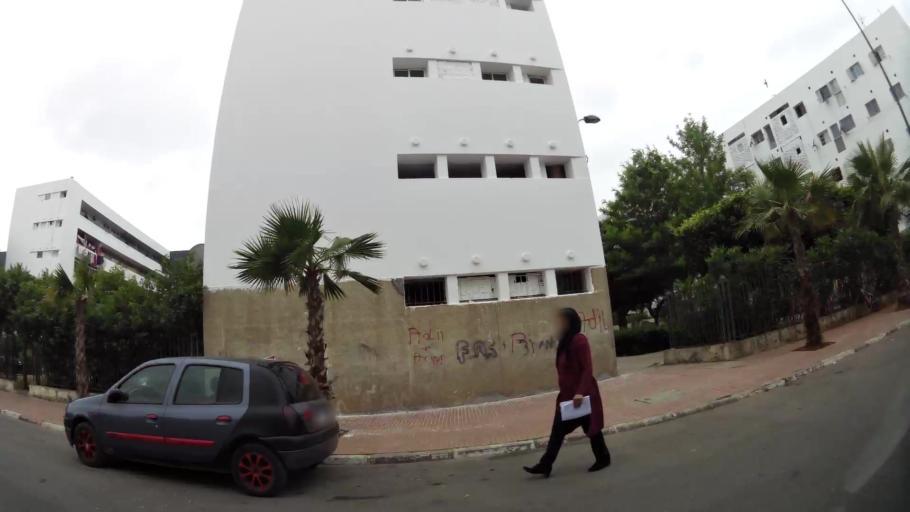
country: MA
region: Rabat-Sale-Zemmour-Zaer
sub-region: Rabat
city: Rabat
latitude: 34.0077
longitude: -6.8583
